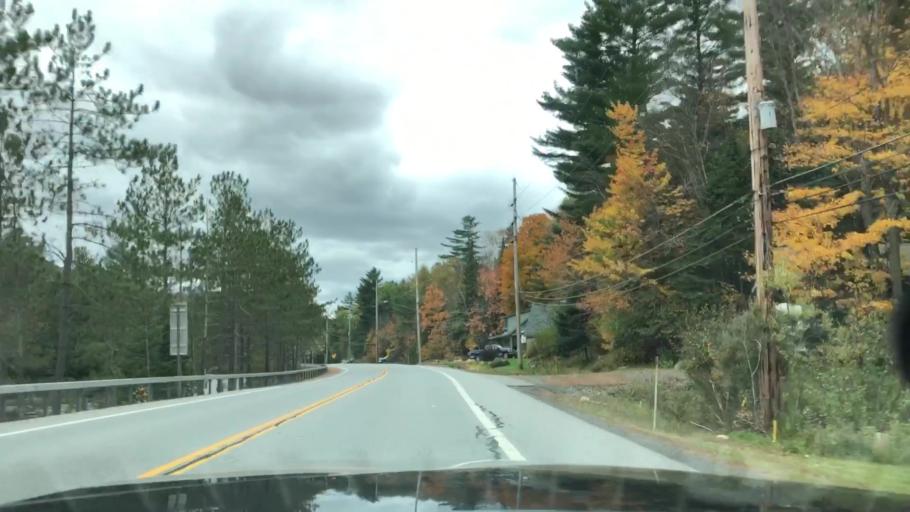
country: US
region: New York
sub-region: Franklin County
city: Tupper Lake
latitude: 43.9710
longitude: -74.4043
